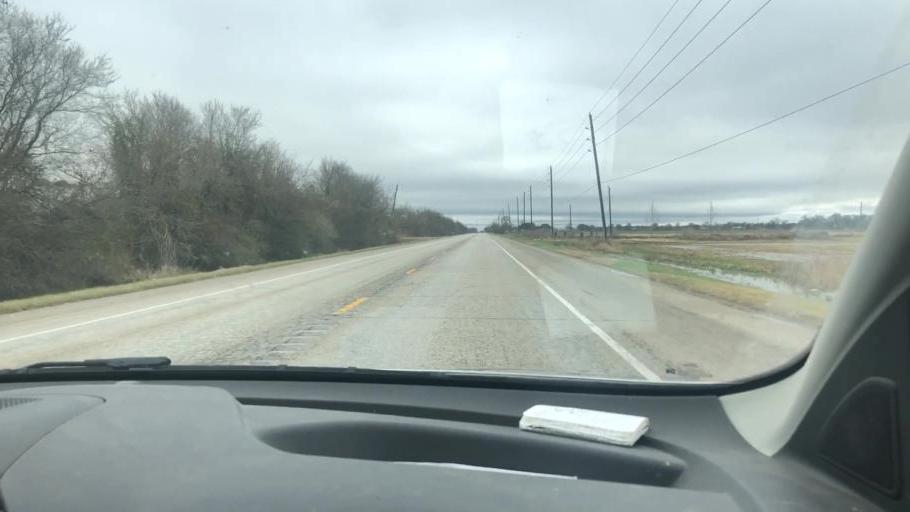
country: US
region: Texas
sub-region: Wharton County
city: Wharton
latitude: 29.2778
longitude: -96.0645
